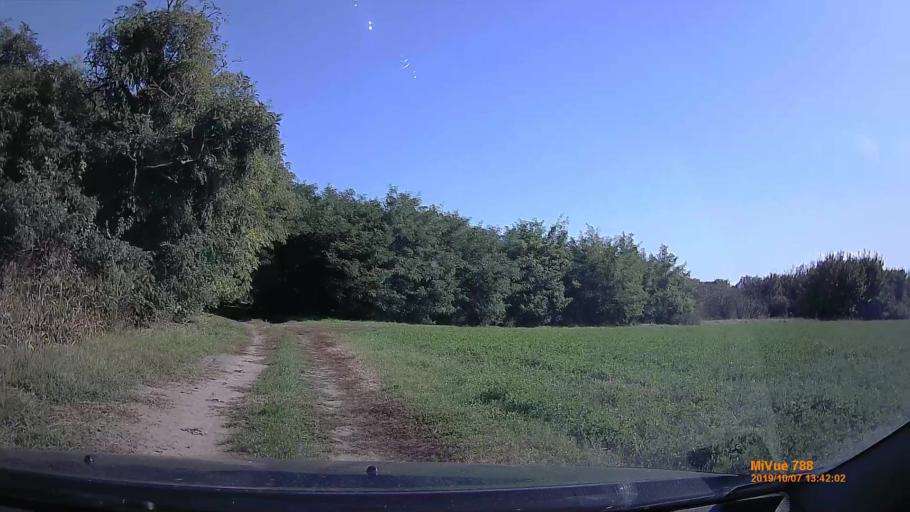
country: HU
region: Jasz-Nagykun-Szolnok
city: Cserkeszolo
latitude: 46.8819
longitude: 20.1942
